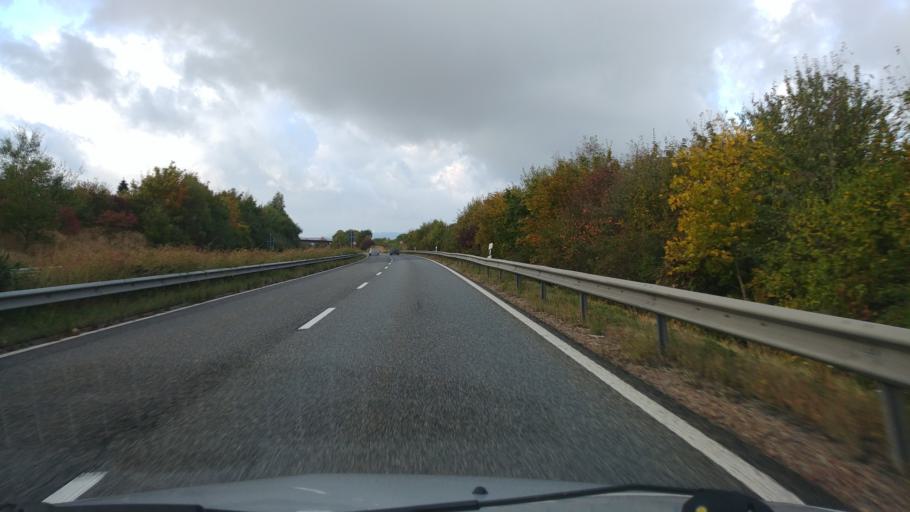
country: DE
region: Rheinland-Pfalz
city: Argenthal
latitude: 49.9786
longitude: 7.6013
